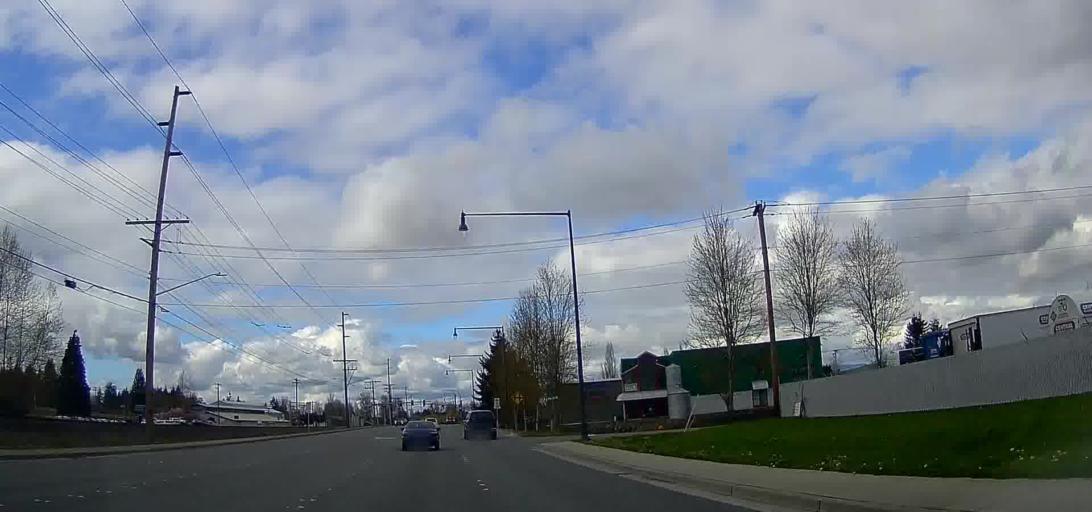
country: US
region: Washington
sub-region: Snohomish County
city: Smokey Point
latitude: 48.1168
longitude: -122.1812
